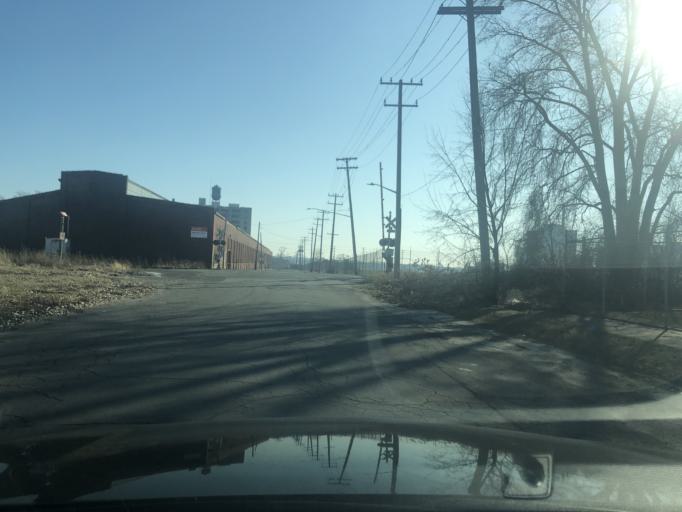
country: US
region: Michigan
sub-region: Wayne County
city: Detroit
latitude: 42.3095
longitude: -83.0898
